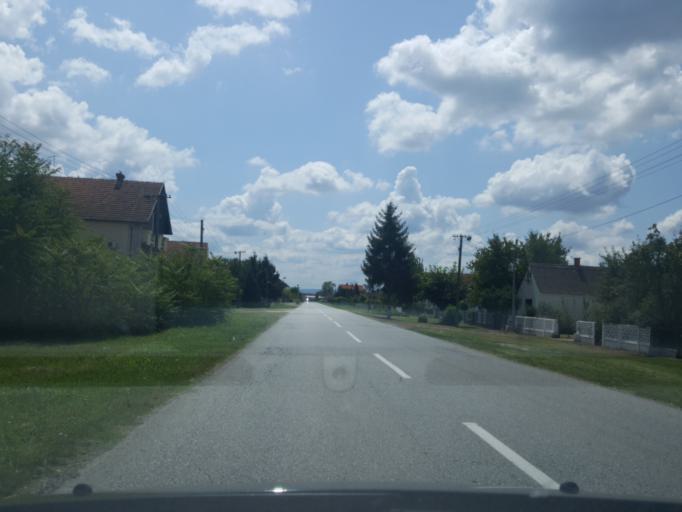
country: RS
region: Central Serbia
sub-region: Macvanski Okrug
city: Bogatic
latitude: 44.8268
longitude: 19.4781
